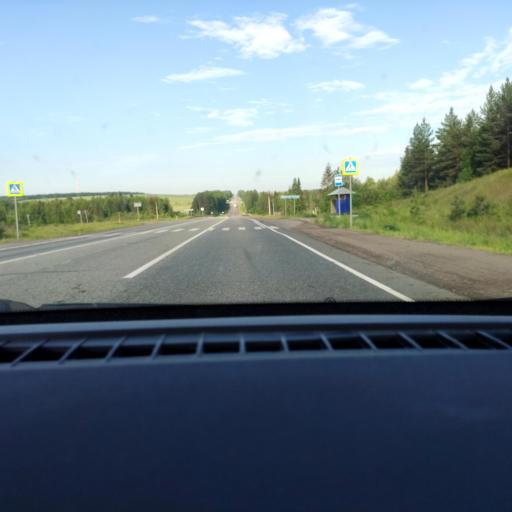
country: RU
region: Udmurtiya
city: Votkinsk
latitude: 56.9618
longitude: 53.6934
